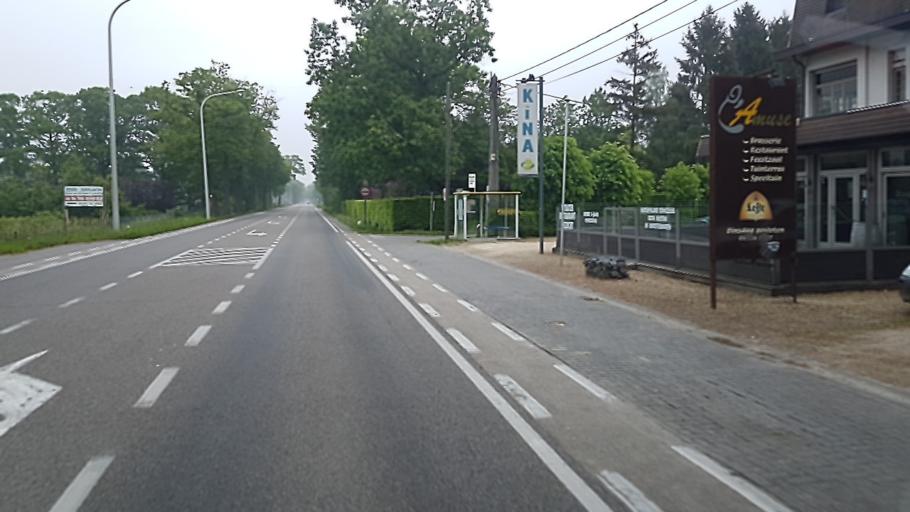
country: BE
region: Flanders
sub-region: Provincie Antwerpen
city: Zoersel
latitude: 51.2784
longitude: 4.6566
